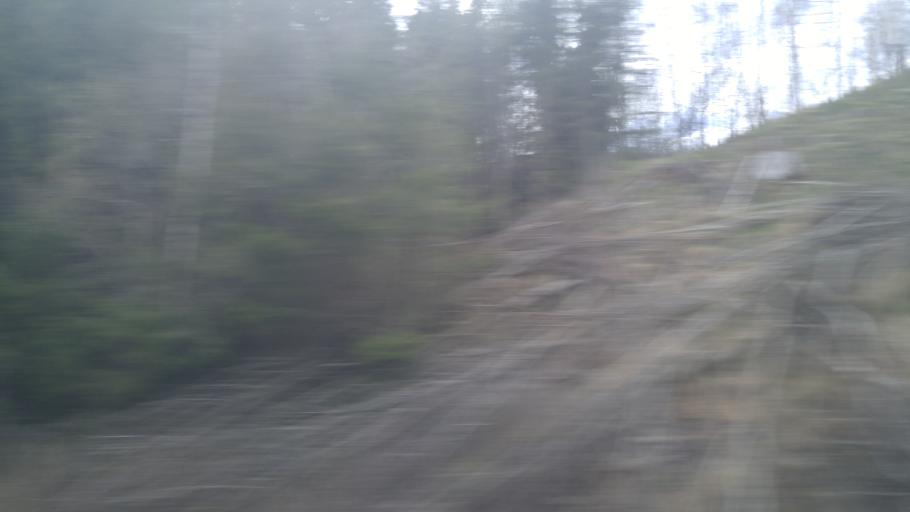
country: NO
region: Akershus
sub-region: Eidsvoll
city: Eidsvoll
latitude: 60.3613
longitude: 11.2449
